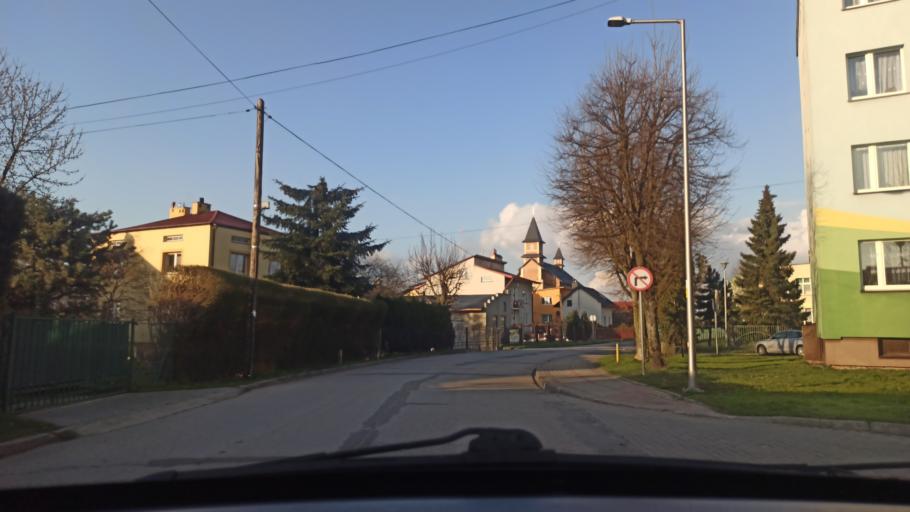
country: PL
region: Subcarpathian Voivodeship
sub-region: Powiat jaroslawski
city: Radymno
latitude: 49.9458
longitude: 22.8257
